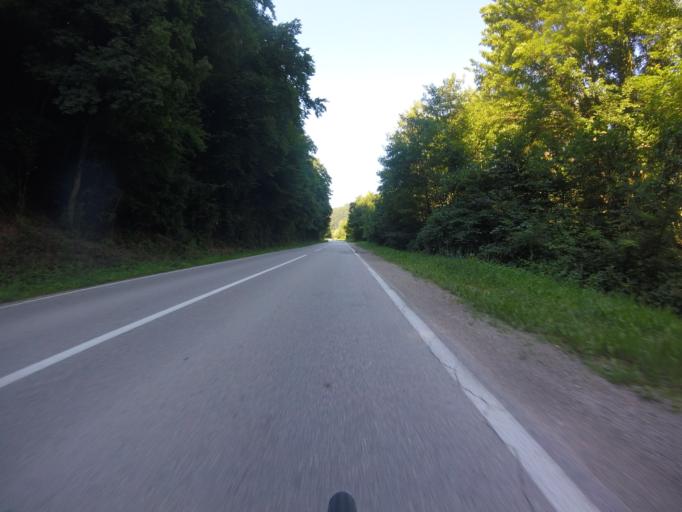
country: HR
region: Zagrebacka
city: Bregana
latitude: 45.8371
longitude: 15.6608
